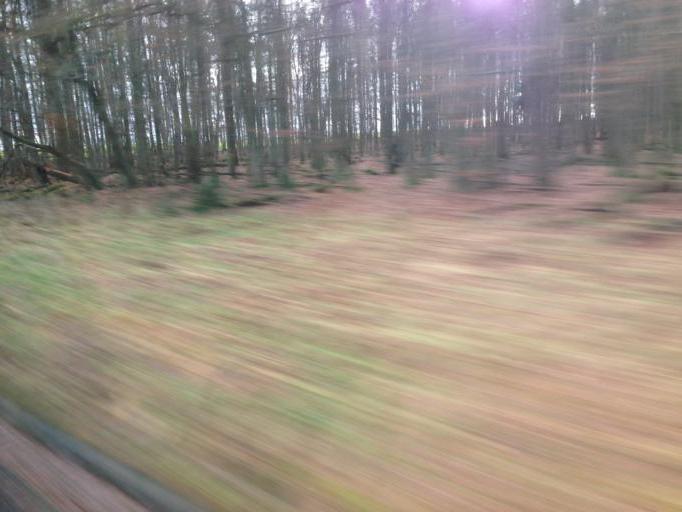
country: DE
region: Hesse
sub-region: Regierungsbezirk Giessen
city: Lich
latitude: 50.5081
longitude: 8.8413
